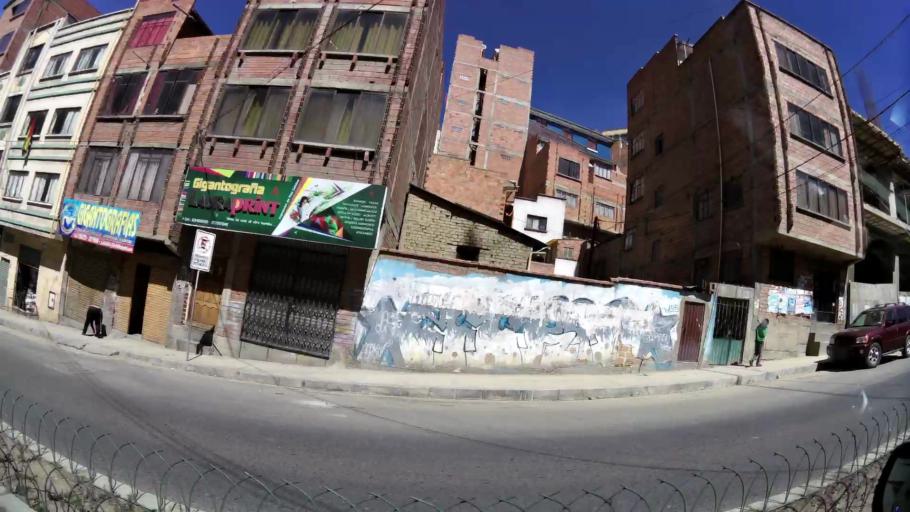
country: BO
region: La Paz
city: La Paz
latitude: -16.4931
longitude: -68.1464
